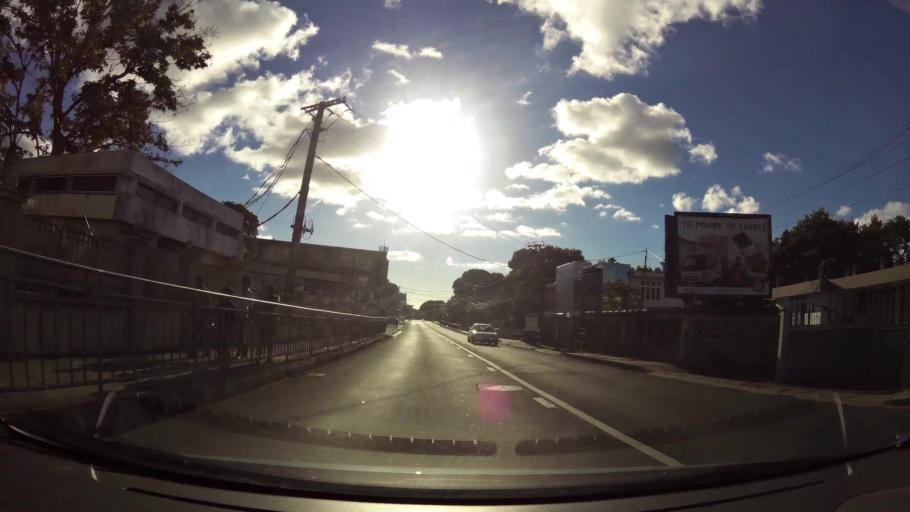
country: MU
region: Plaines Wilhems
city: Ebene
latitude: -20.2482
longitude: 57.4825
